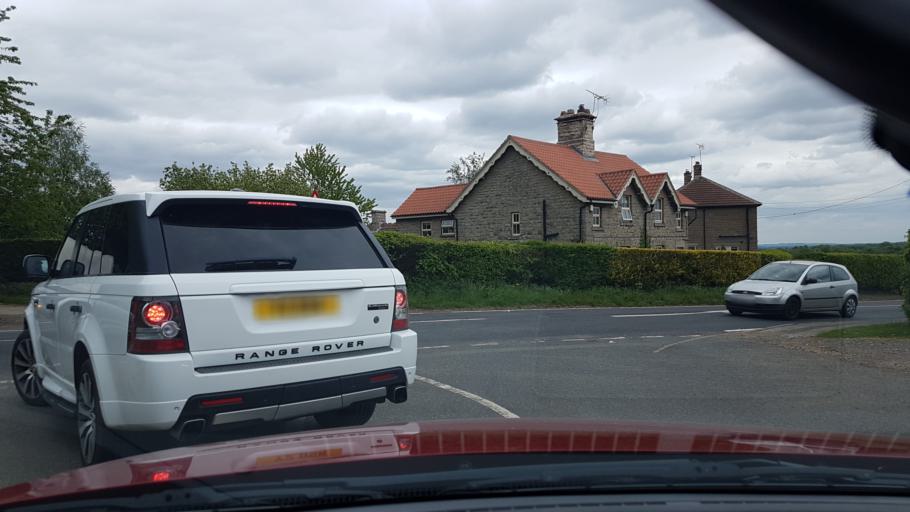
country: GB
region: England
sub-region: Rotherham
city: Maltby
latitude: 53.4065
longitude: -1.1836
